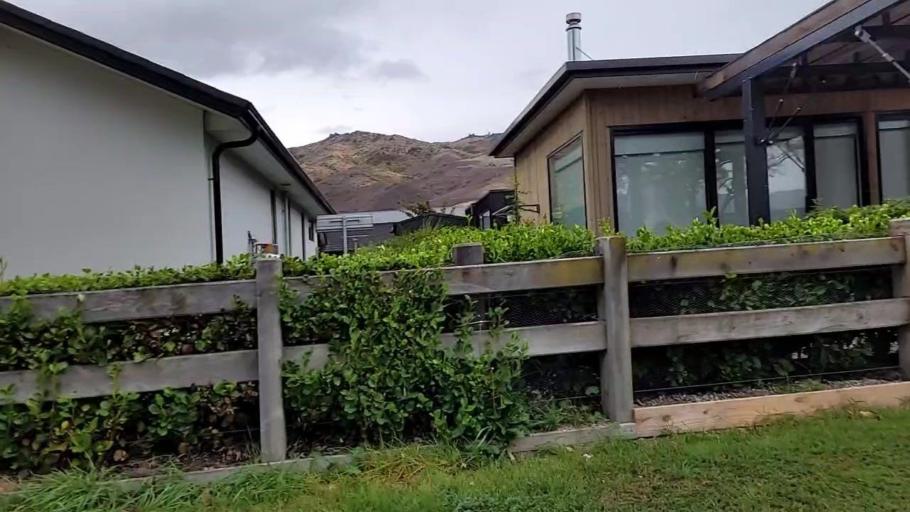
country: NZ
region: Otago
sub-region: Queenstown-Lakes District
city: Wanaka
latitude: -45.0376
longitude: 169.2162
